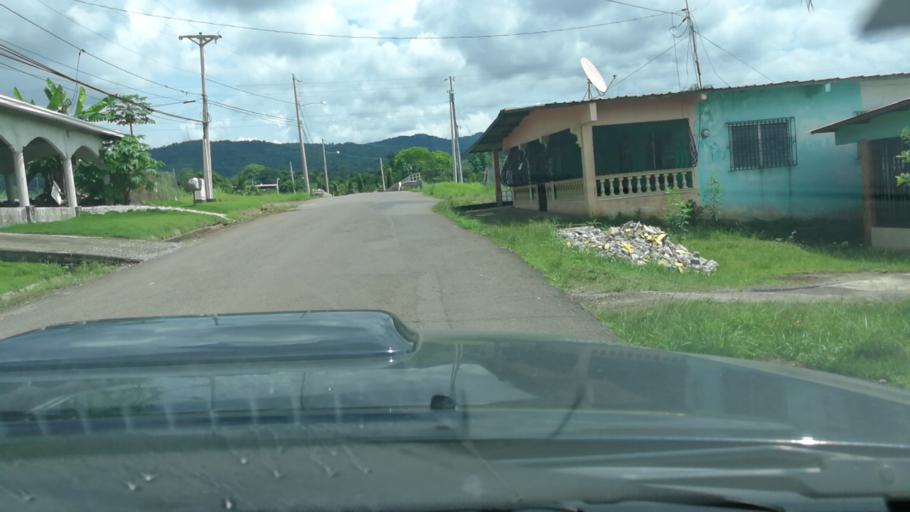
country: PA
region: Panama
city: Tocumen
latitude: 9.1031
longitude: -79.4119
